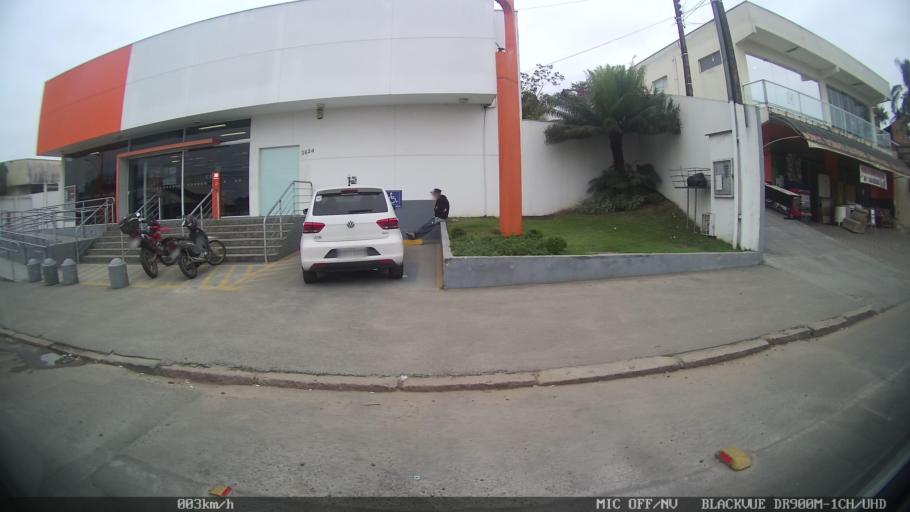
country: BR
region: Santa Catarina
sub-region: Joinville
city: Joinville
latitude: -26.3408
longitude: -48.8180
